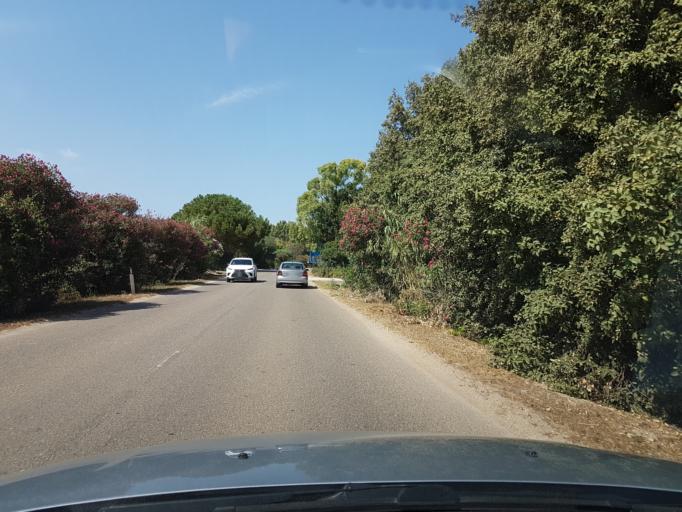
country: IT
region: Sardinia
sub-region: Provincia di Oristano
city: Cabras
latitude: 39.9259
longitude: 8.4546
